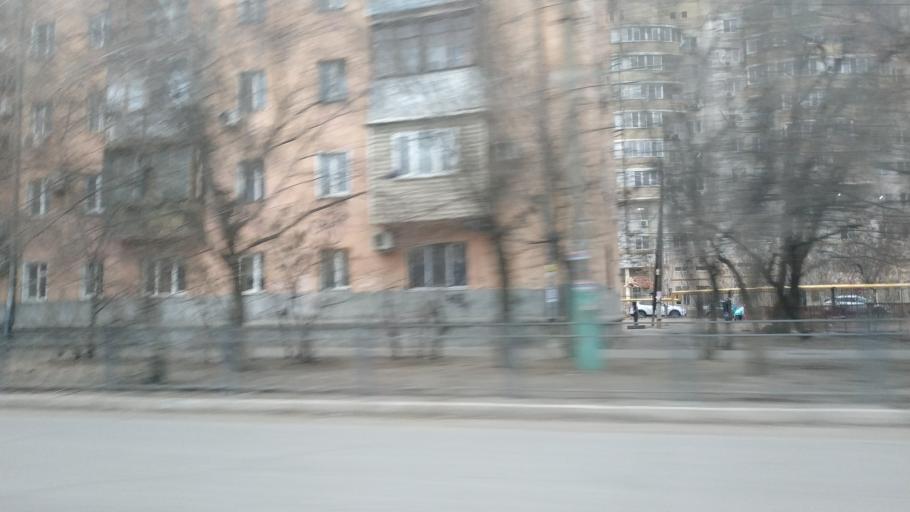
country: RU
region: Astrakhan
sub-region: Gorod Astrakhan'
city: Astrakhan'
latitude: 46.3338
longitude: 48.0143
